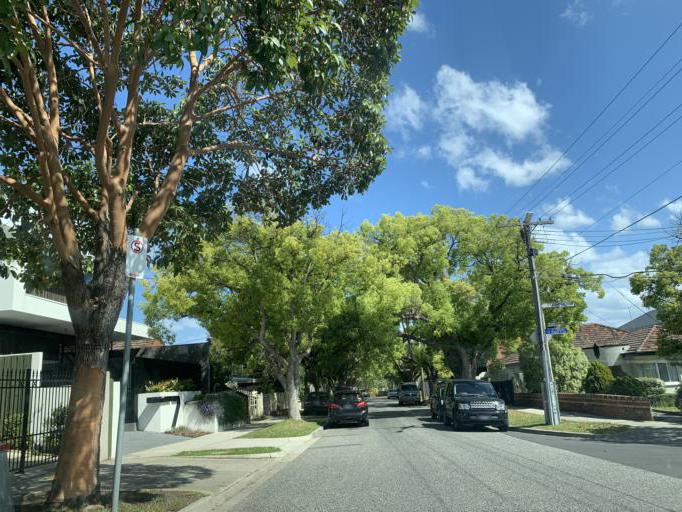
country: AU
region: Victoria
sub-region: Bayside
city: North Brighton
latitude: -37.9166
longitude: 145.0158
